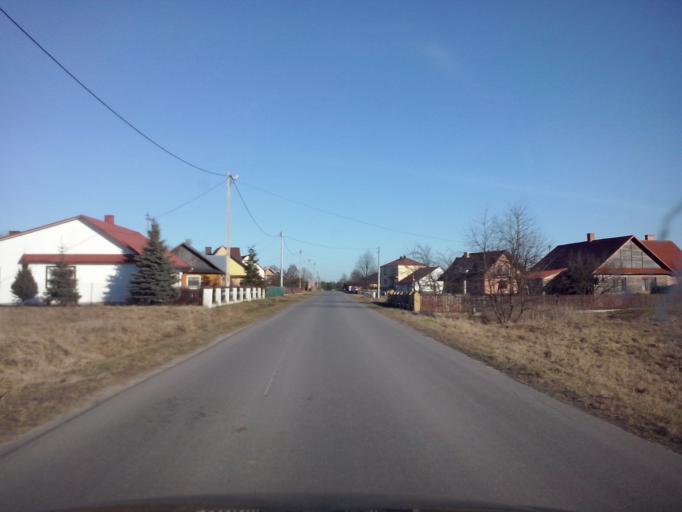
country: PL
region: Subcarpathian Voivodeship
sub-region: Powiat nizanski
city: Harasiuki
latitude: 50.5235
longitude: 22.4564
